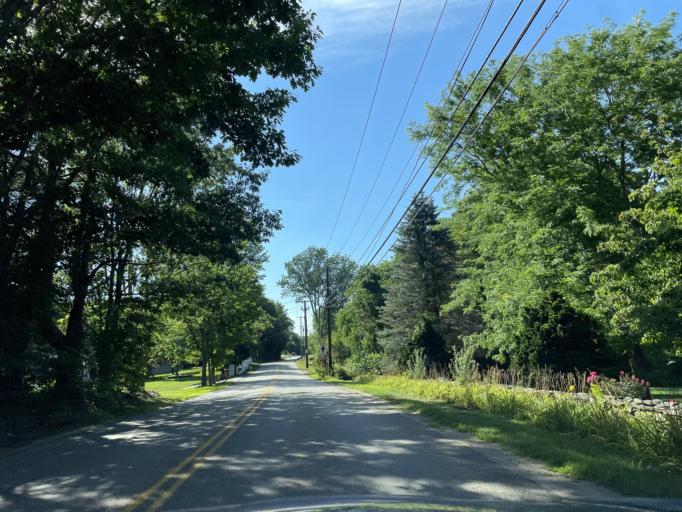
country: US
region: Massachusetts
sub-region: Worcester County
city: Charlton
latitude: 42.1316
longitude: -71.9335
